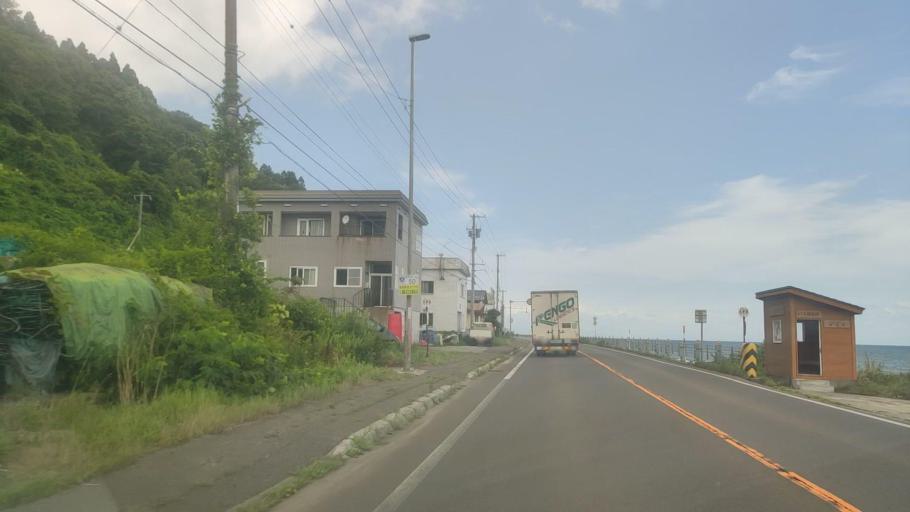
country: JP
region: Hokkaido
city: Nanae
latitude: 42.1418
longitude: 140.5024
